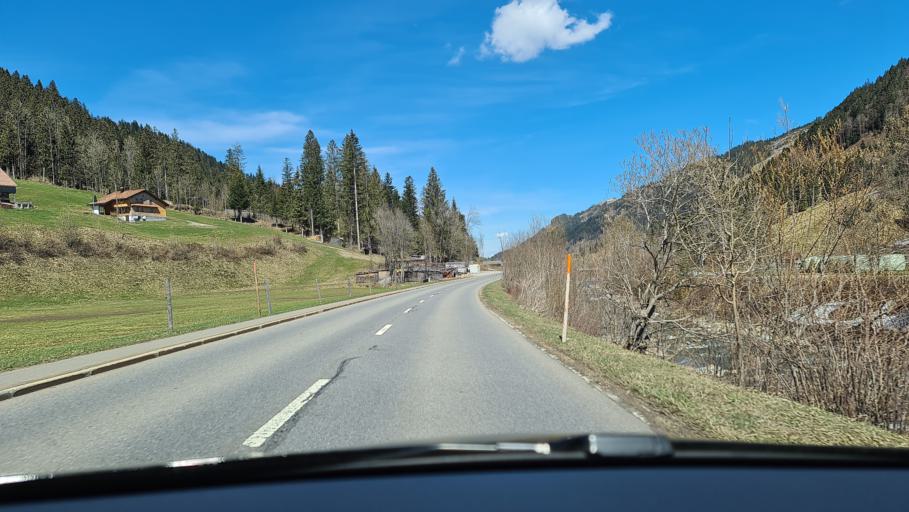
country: CH
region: Schwyz
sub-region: Bezirk Schwyz
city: Rothenthurm
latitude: 47.0604
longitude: 8.7118
